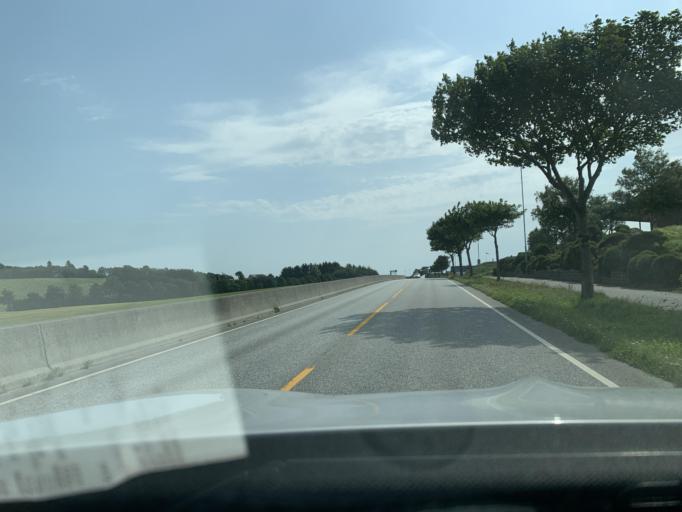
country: NO
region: Rogaland
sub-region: Klepp
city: Kleppe
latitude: 58.7642
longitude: 5.6257
